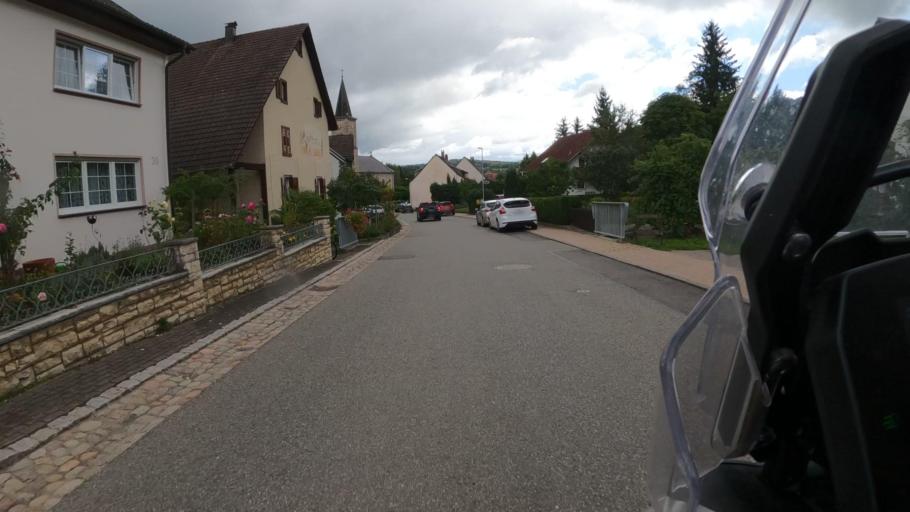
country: DE
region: Baden-Wuerttemberg
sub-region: Freiburg Region
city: Eggingen
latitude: 47.7018
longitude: 8.3847
